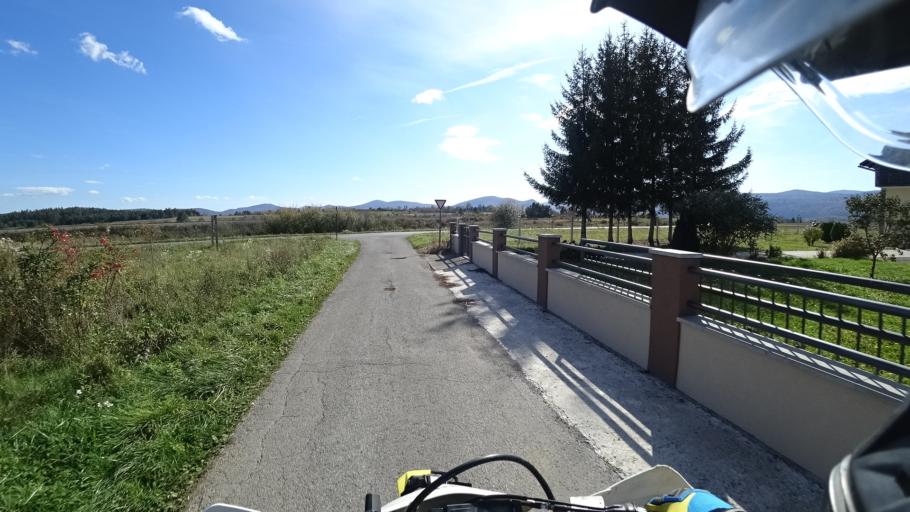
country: HR
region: Karlovacka
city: Plaski
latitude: 45.1089
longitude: 15.3601
